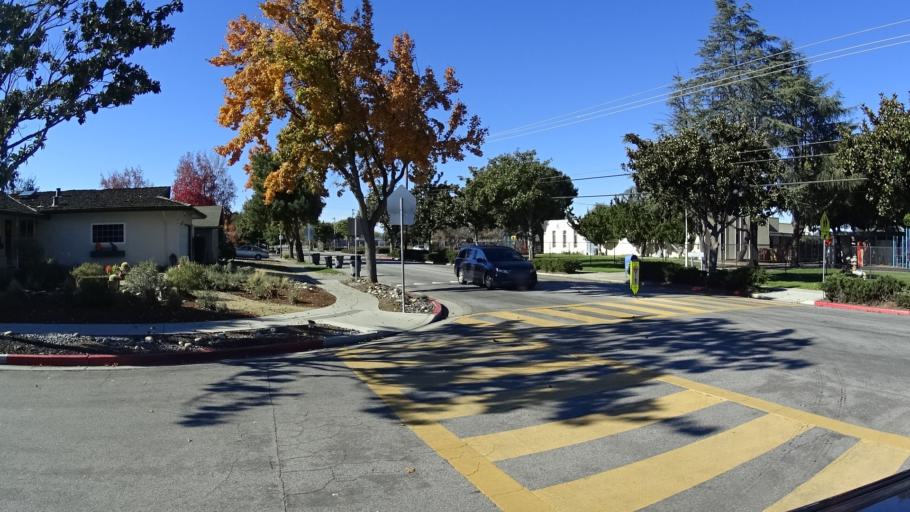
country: US
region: California
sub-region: Santa Clara County
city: Cupertino
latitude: 37.3452
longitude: -122.0035
